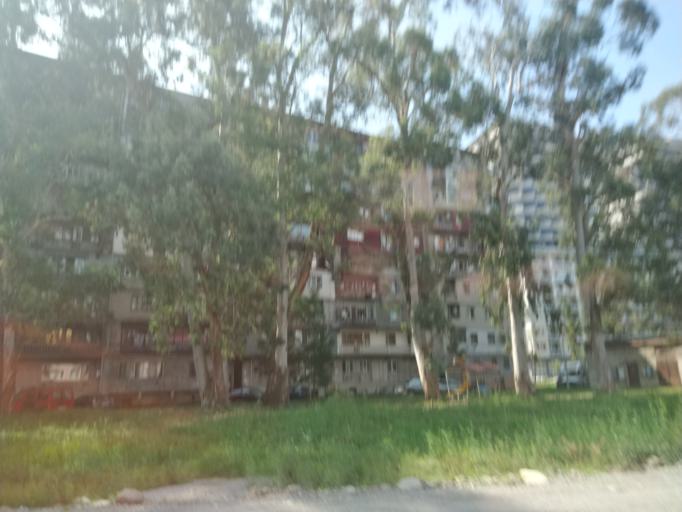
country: GE
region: Ajaria
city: Batumi
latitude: 41.6327
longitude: 41.6063
